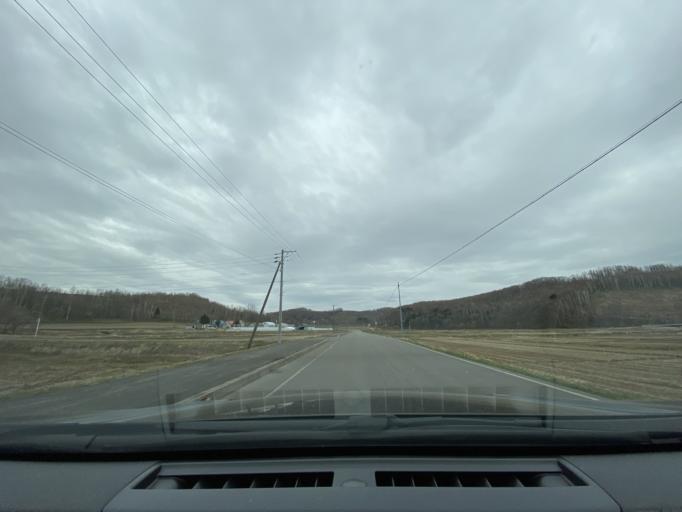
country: JP
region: Hokkaido
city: Nayoro
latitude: 44.0876
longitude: 142.4218
